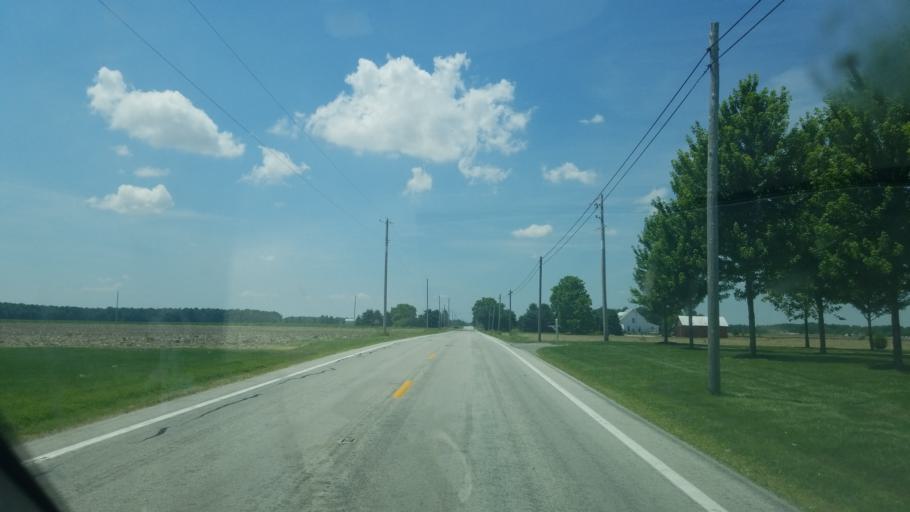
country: US
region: Ohio
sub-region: Hancock County
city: Arlington
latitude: 40.8917
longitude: -83.5969
